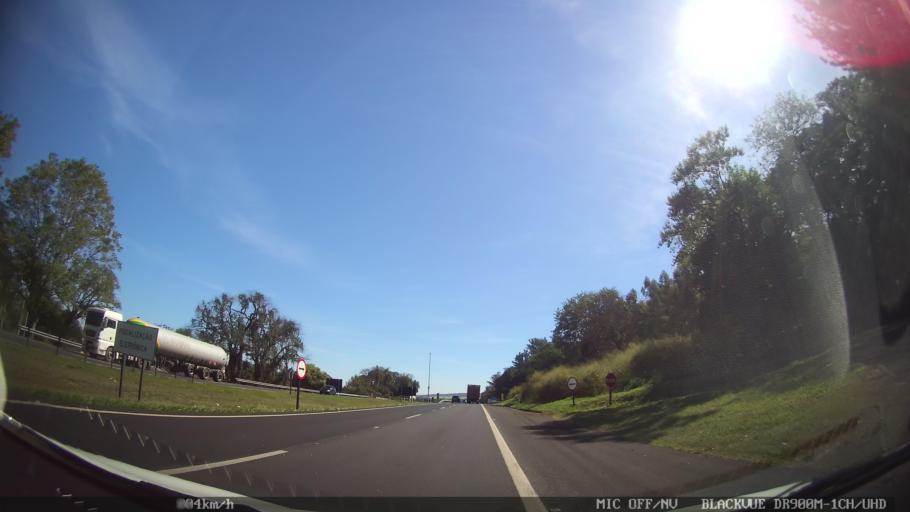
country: BR
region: Sao Paulo
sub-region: Santa Rita Do Passa Quatro
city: Santa Rita do Passa Quatro
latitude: -21.7495
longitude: -47.5714
